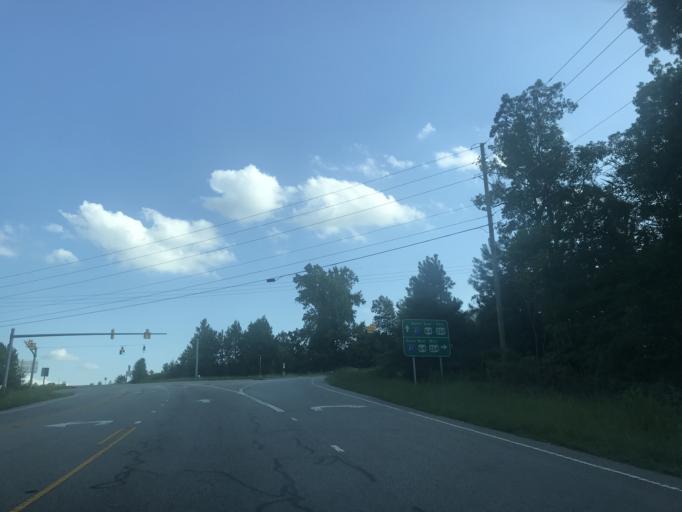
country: US
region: North Carolina
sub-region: Wake County
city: Knightdale
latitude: 35.7706
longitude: -78.5230
